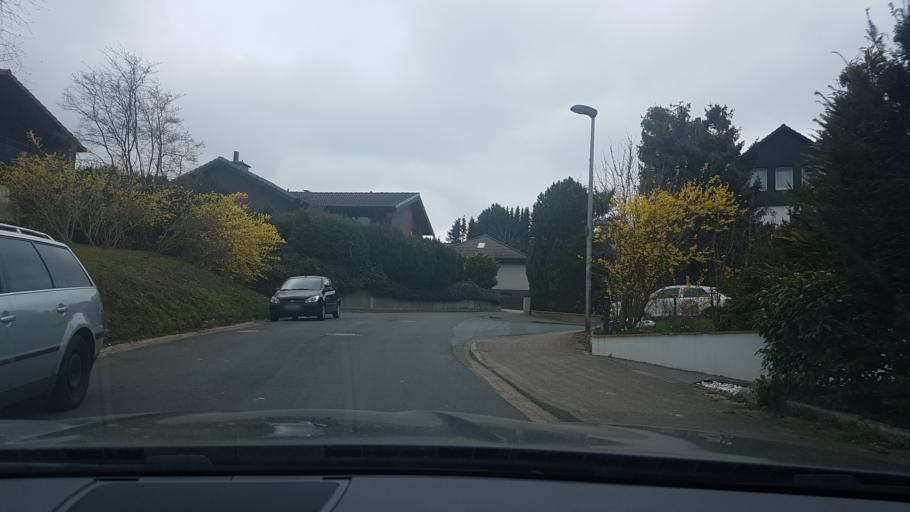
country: DE
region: Lower Saxony
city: Hameln
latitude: 52.1394
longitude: 9.3759
